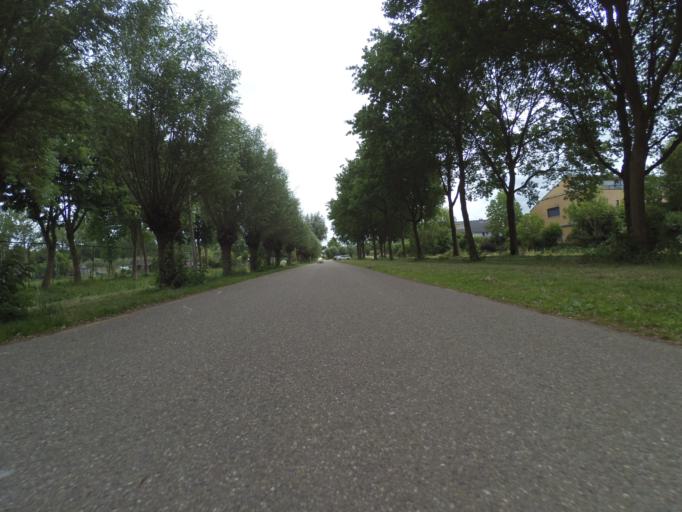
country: NL
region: South Holland
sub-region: Gemeente Leerdam
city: Leerdam
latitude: 51.8989
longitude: 5.0779
